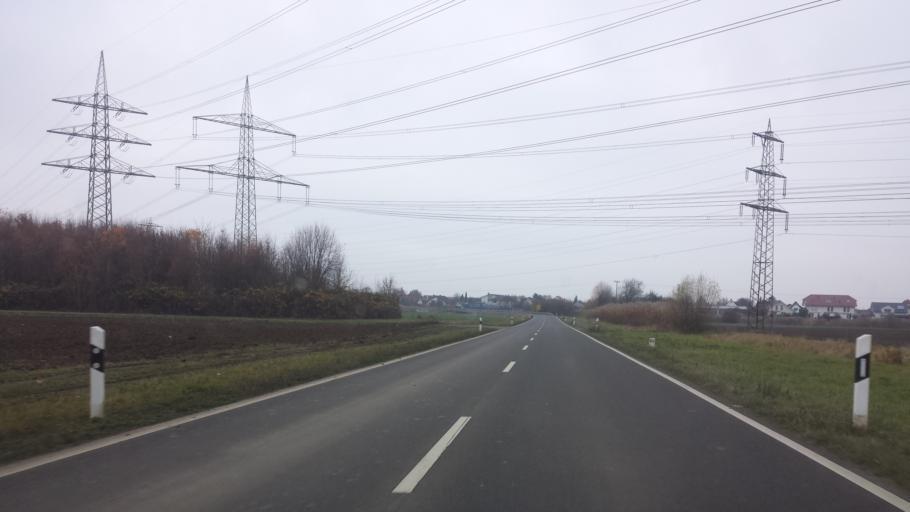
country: DE
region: Rheinland-Pfalz
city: Worms
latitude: 49.6542
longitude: 8.3970
